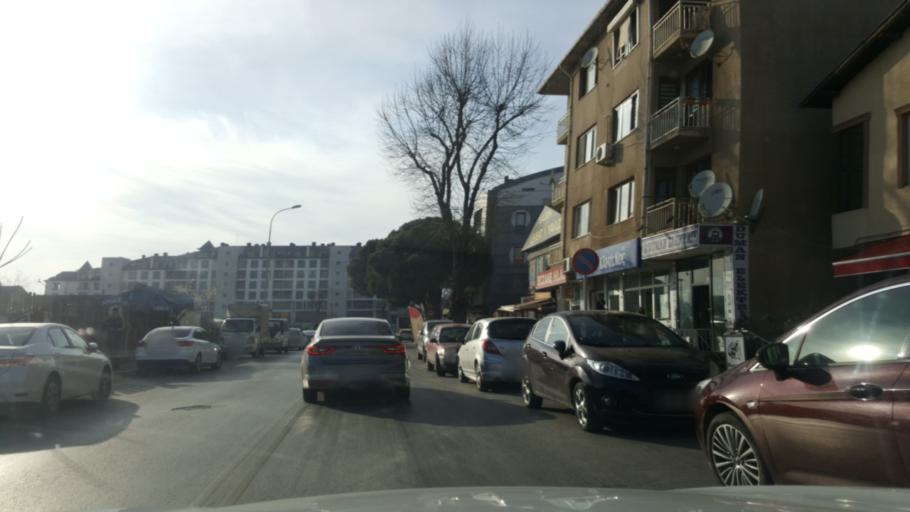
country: TR
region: Istanbul
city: Icmeler
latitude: 40.8177
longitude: 29.3026
